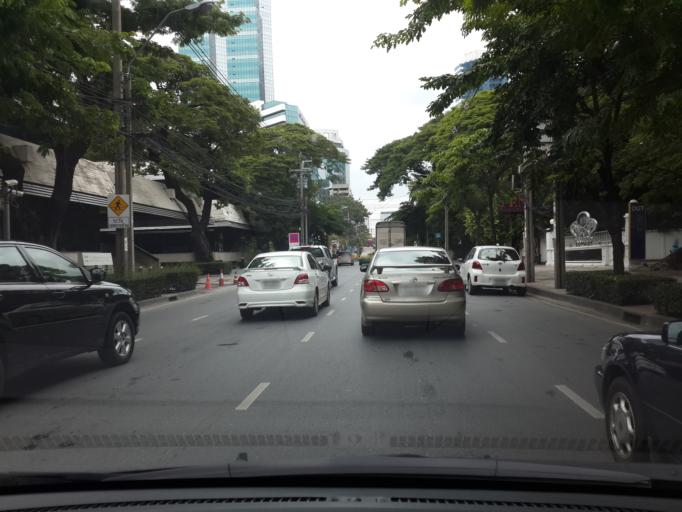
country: TH
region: Bangkok
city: Ratchathewi
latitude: 13.7459
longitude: 100.5480
